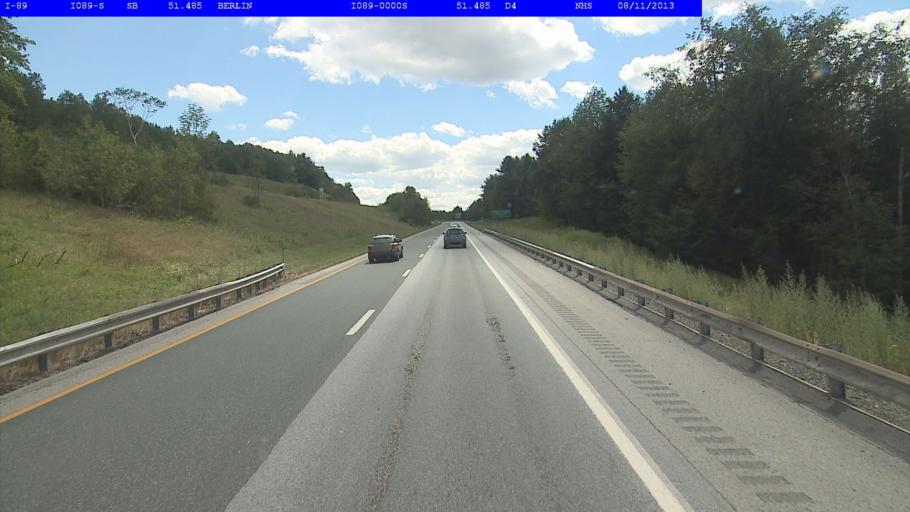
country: US
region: Vermont
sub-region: Washington County
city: Montpelier
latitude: 44.2328
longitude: -72.5860
